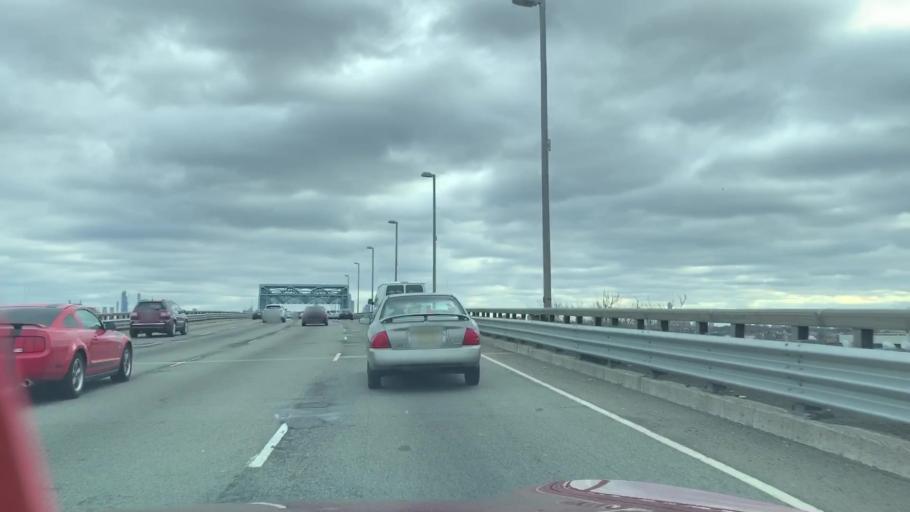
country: US
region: New Jersey
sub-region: Hudson County
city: Secaucus
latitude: 40.7996
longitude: -74.0704
